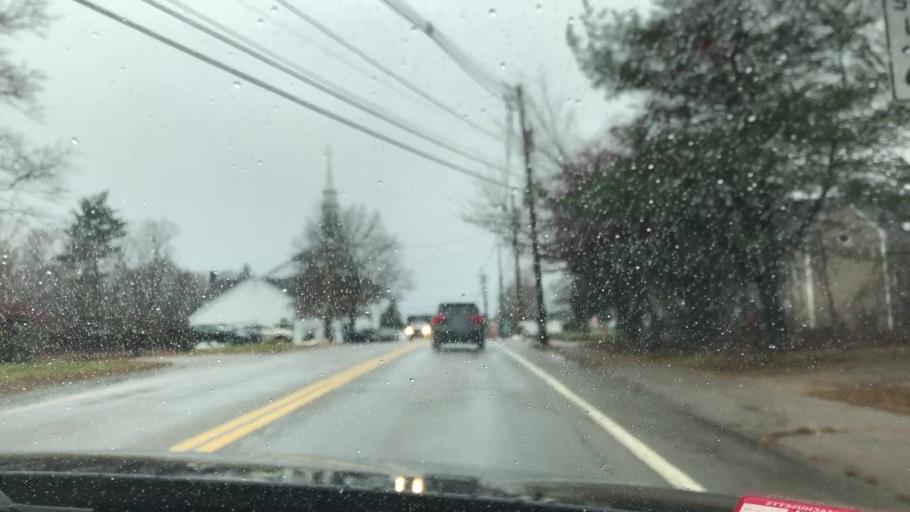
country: US
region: Massachusetts
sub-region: Norfolk County
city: Wrentham
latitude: 42.0681
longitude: -71.3263
